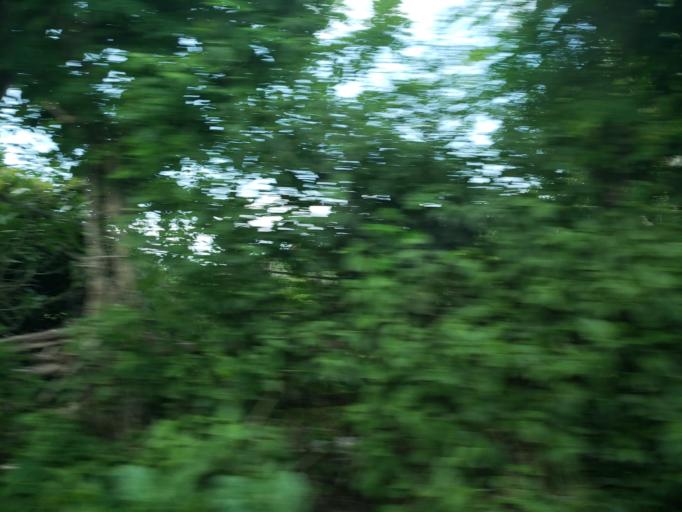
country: ID
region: Bali
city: Kangin
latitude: -8.8407
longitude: 115.1520
